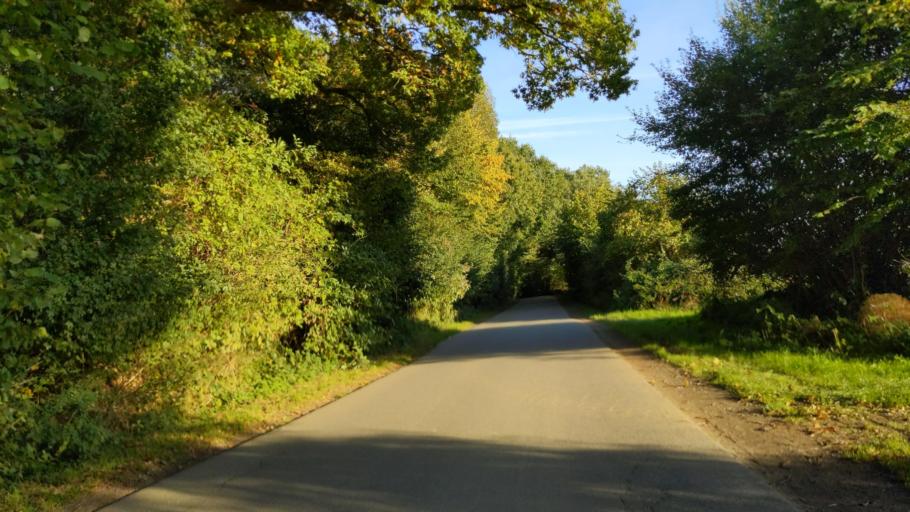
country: DE
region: Schleswig-Holstein
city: Susel
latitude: 54.0854
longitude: 10.6680
